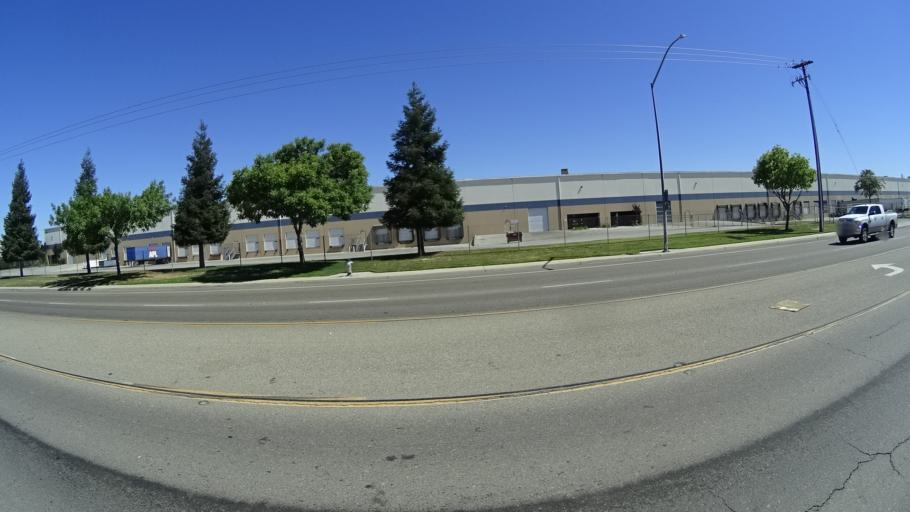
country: US
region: California
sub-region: Fresno County
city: Easton
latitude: 36.6920
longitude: -119.7804
